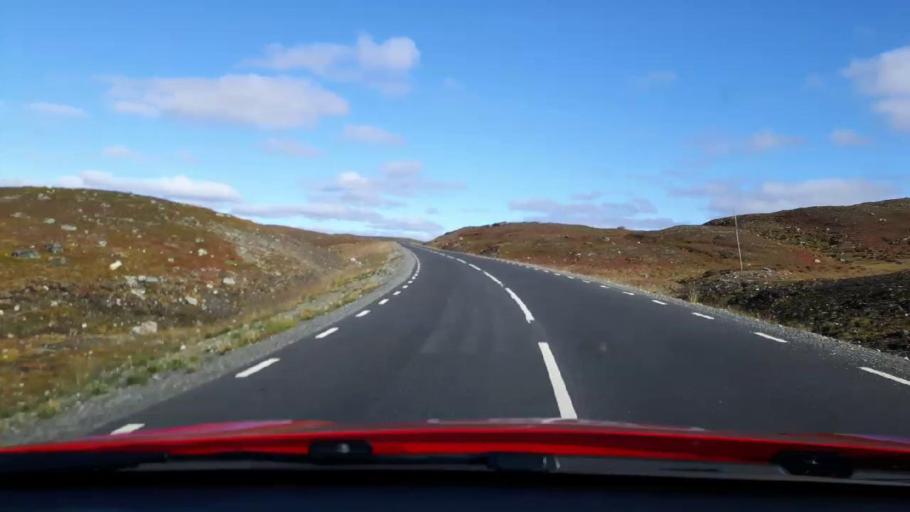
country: NO
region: Nordland
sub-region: Hattfjelldal
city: Hattfjelldal
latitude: 65.0502
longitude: 14.3429
